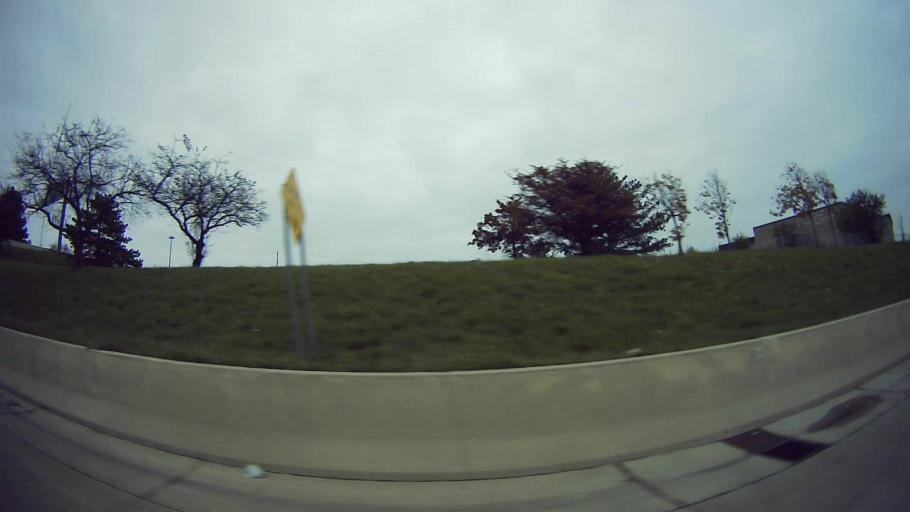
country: US
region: Michigan
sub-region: Oakland County
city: Southfield
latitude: 42.4562
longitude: -83.2198
